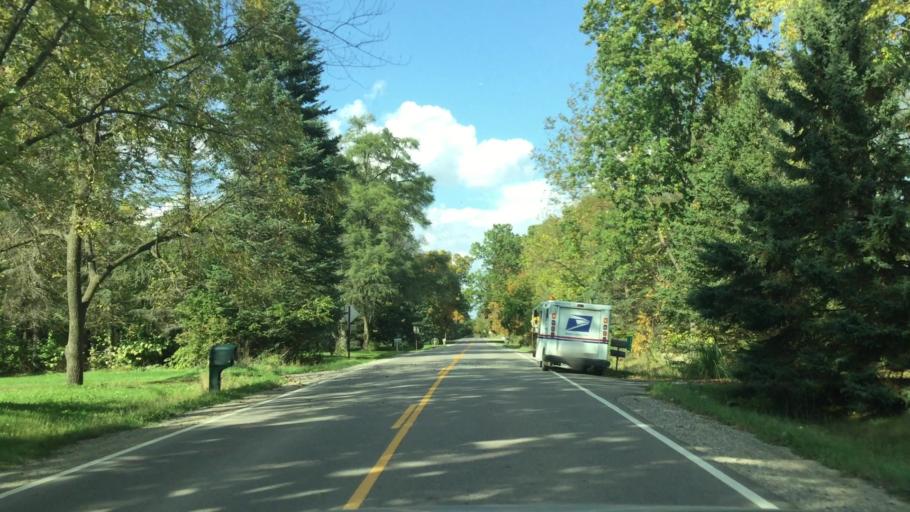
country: US
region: Michigan
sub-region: Oakland County
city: Milford
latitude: 42.6469
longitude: -83.7001
